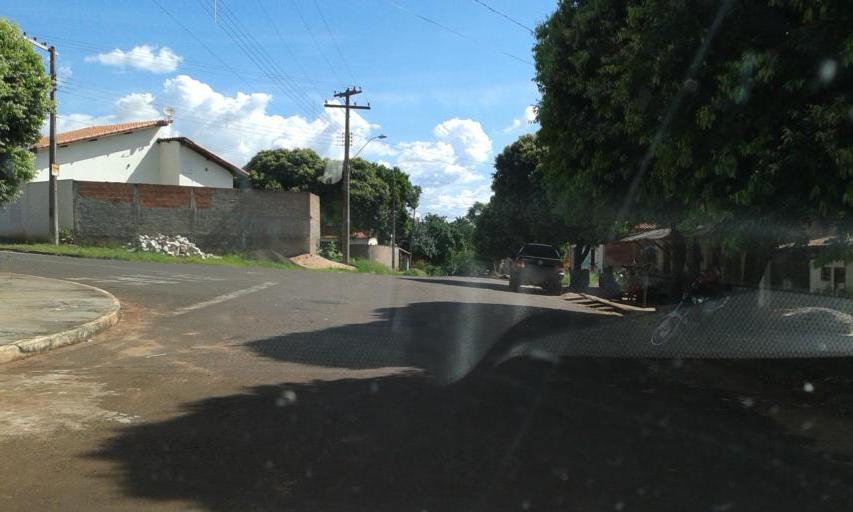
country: BR
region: Minas Gerais
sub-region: Ituiutaba
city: Ituiutaba
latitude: -18.9625
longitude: -49.4721
